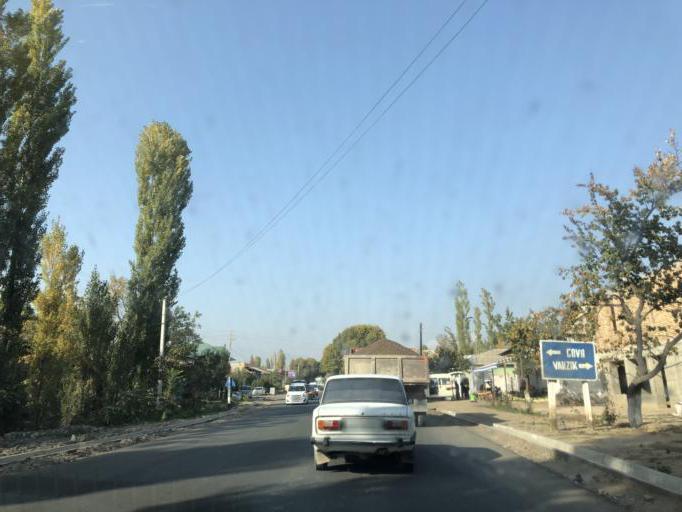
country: UZ
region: Namangan
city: Chust Shahri
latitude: 41.0711
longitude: 71.2046
